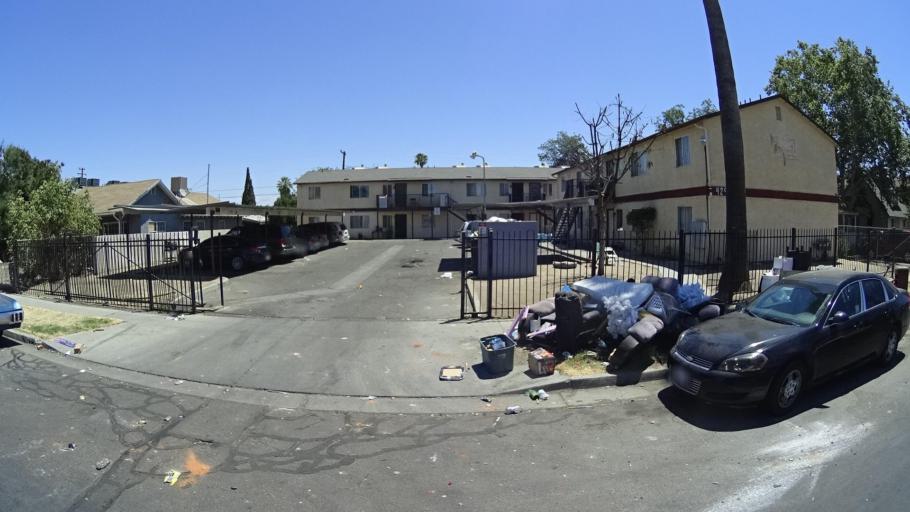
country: US
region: California
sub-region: Fresno County
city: Fresno
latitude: 36.7389
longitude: -119.7439
